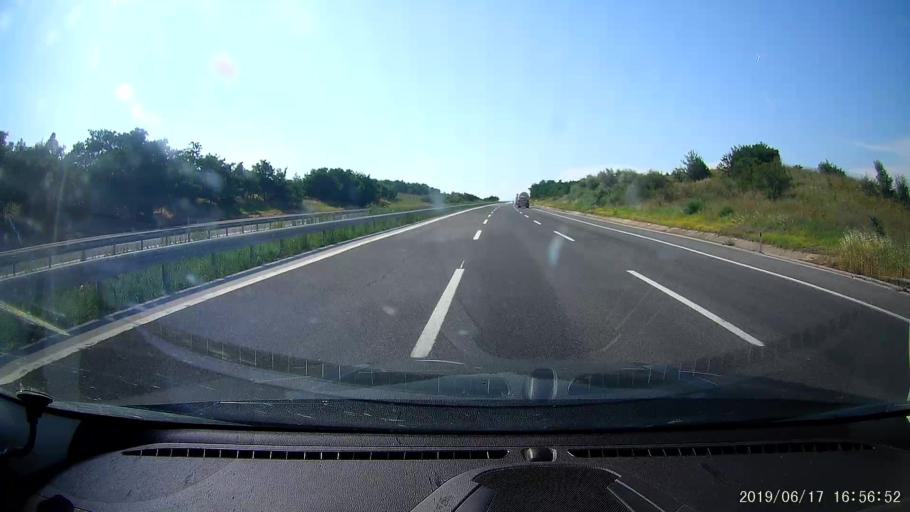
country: TR
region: Edirne
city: Haskoy
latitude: 41.5921
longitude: 26.9264
